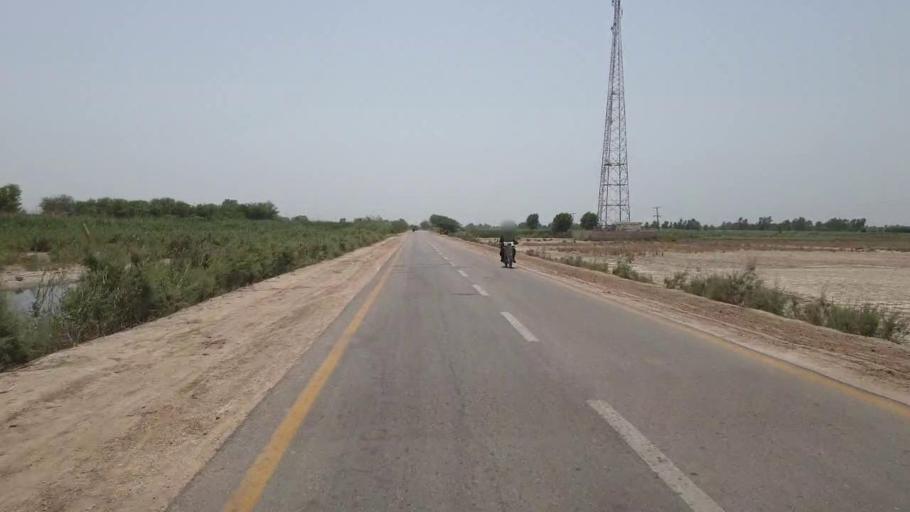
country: PK
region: Sindh
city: Moro
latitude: 26.6021
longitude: 68.0652
